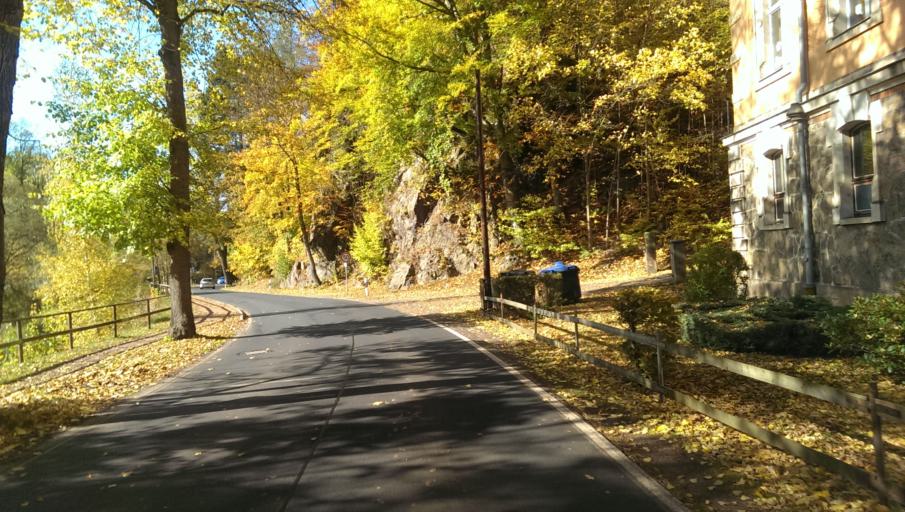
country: DE
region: Saxony
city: Barenstein
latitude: 50.7857
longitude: 13.8236
